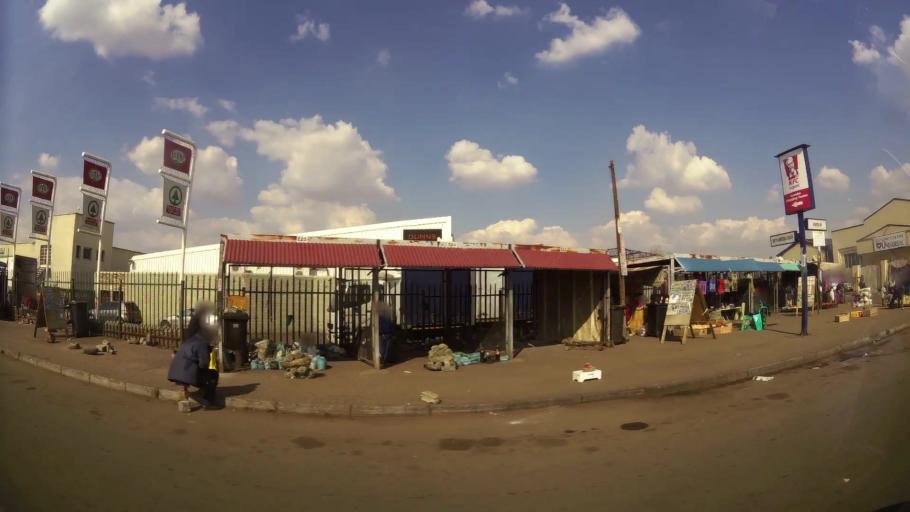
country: ZA
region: Gauteng
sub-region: Ekurhuleni Metropolitan Municipality
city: Germiston
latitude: -26.3274
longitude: 28.1445
